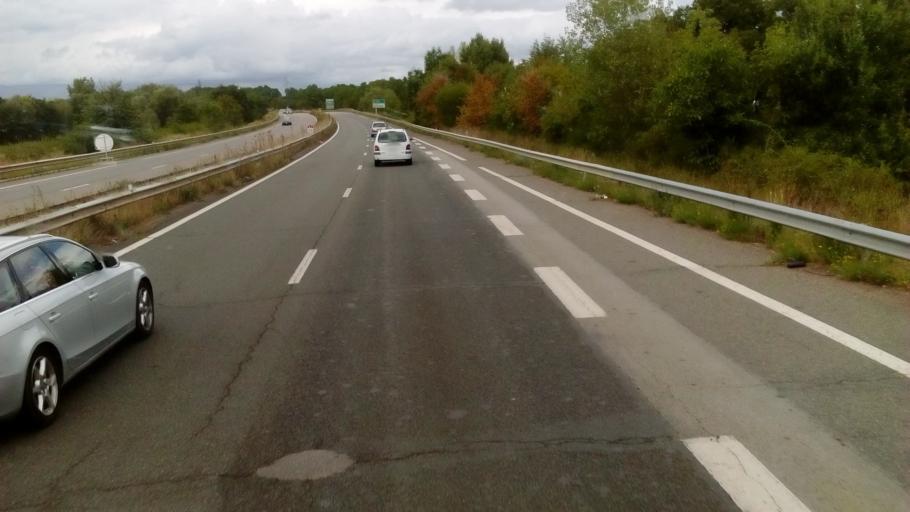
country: FR
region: Rhone-Alpes
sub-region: Departement de la Loire
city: Le Coteau
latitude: 46.0380
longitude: 4.0993
